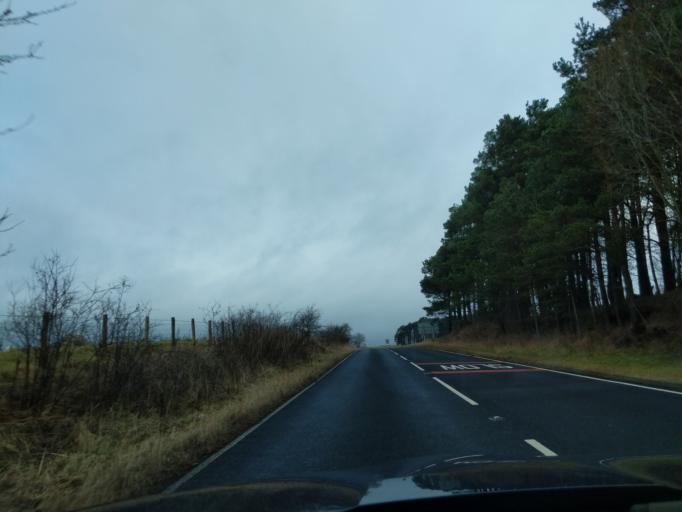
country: GB
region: England
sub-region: Northumberland
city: Rothley
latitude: 55.1669
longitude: -2.0202
